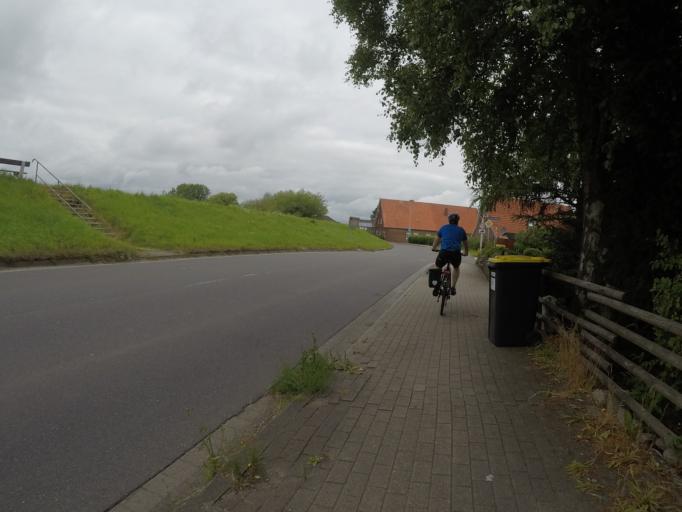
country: DE
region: Lower Saxony
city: Mittelnkirchen
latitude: 53.5409
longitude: 9.6235
